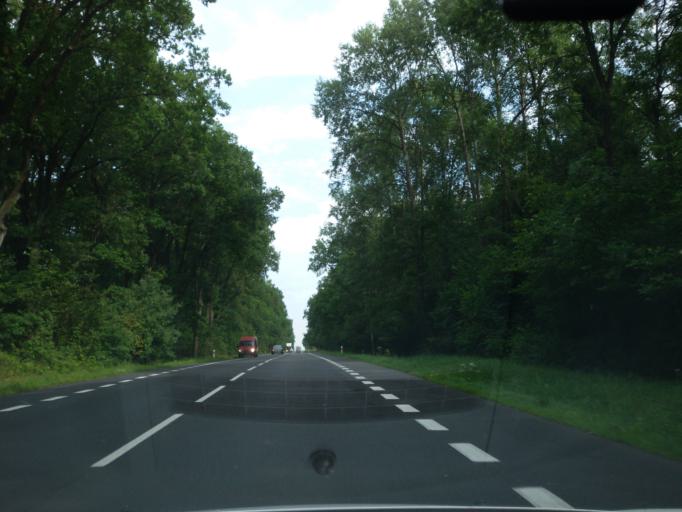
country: PL
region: Lubusz
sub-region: Powiat nowosolski
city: Bytom Odrzanski
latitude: 51.6676
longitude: 15.8049
